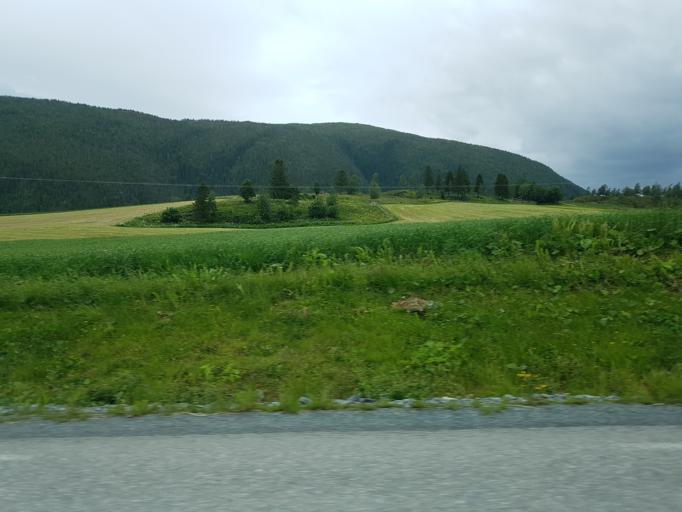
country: NO
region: Nord-Trondelag
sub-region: Levanger
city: Skogn
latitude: 63.6075
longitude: 11.0831
